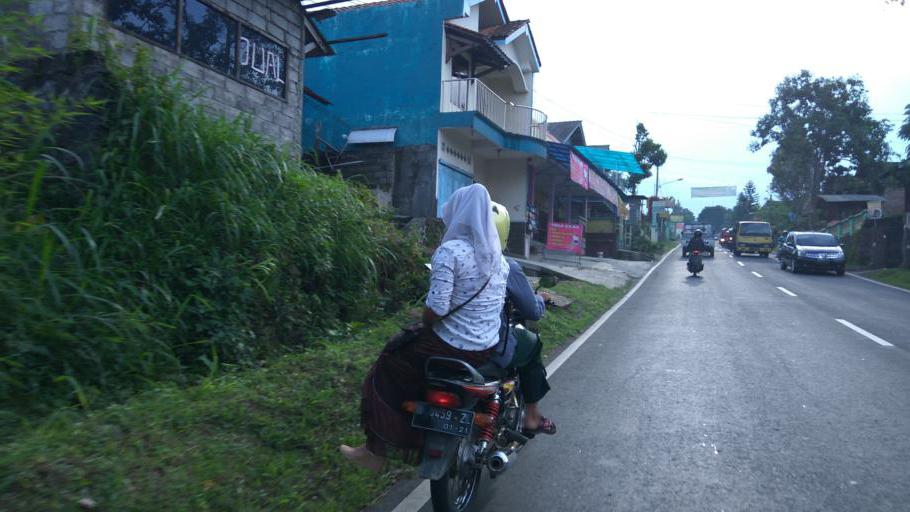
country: ID
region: Central Java
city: Salatiga
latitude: -7.3692
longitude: 110.4527
